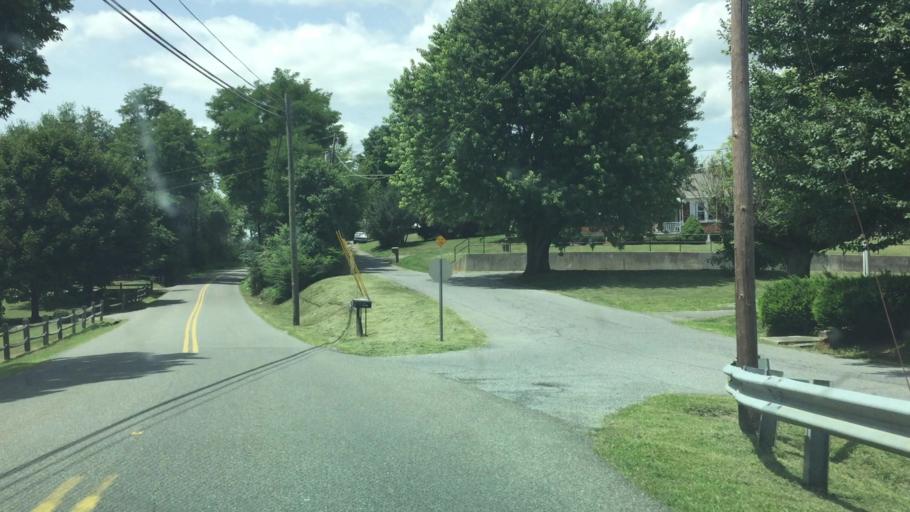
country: US
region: Virginia
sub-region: Wythe County
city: Wytheville
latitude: 36.9579
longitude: -81.0924
